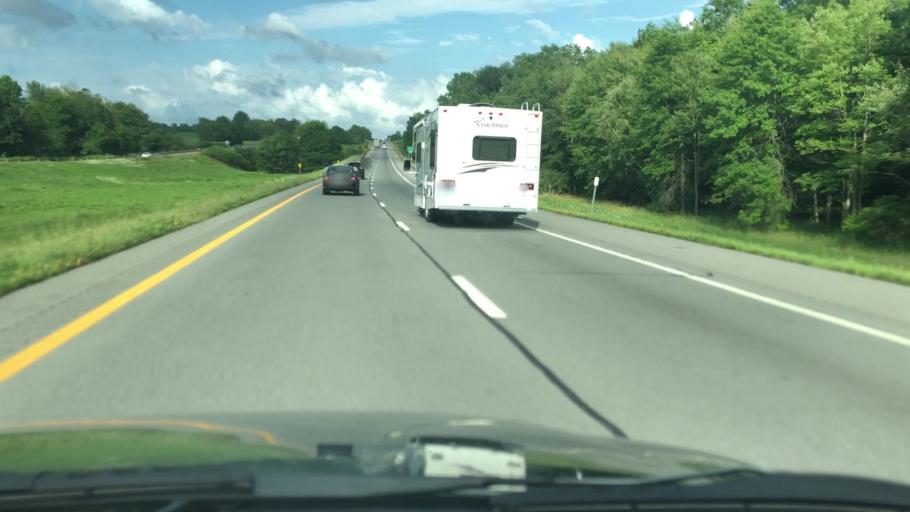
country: US
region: New York
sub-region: Orange County
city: Montgomery
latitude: 41.4978
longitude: -74.2564
